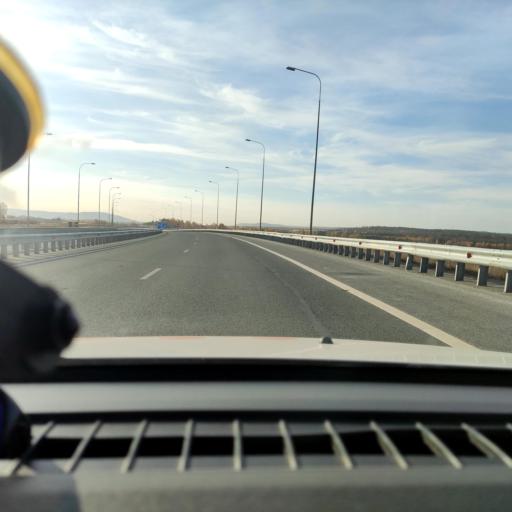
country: RU
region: Samara
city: Bereza
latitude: 53.4986
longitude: 50.1165
